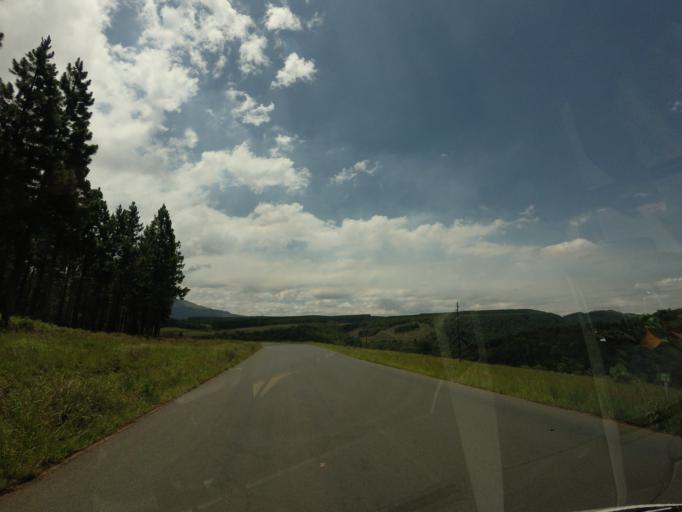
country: ZA
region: Mpumalanga
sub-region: Ehlanzeni District
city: Graksop
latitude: -25.0044
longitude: 30.8226
